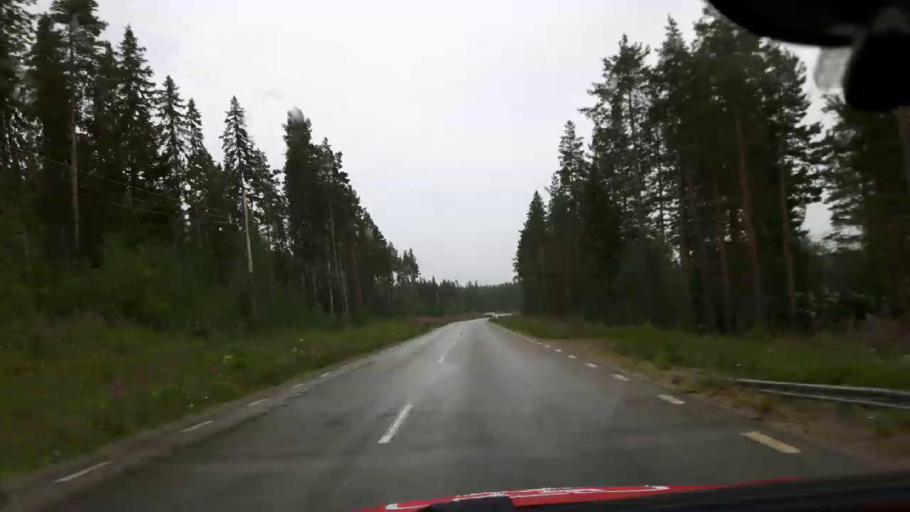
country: SE
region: Jaemtland
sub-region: OEstersunds Kommun
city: Brunflo
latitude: 62.7815
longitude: 15.0117
